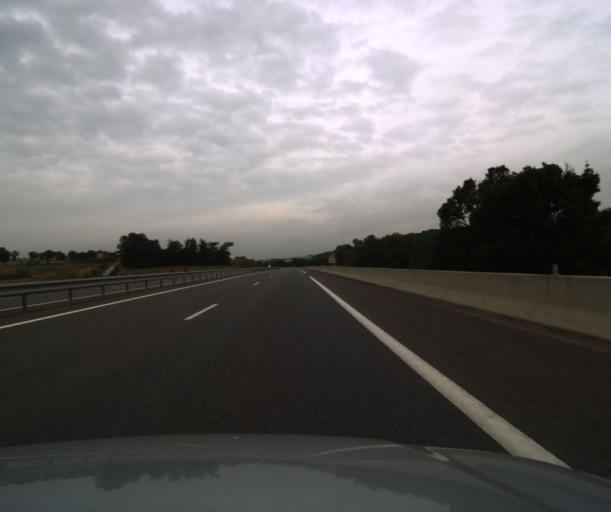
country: FR
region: Midi-Pyrenees
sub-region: Departement du Gers
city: Aubiet
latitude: 43.6578
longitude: 0.7763
